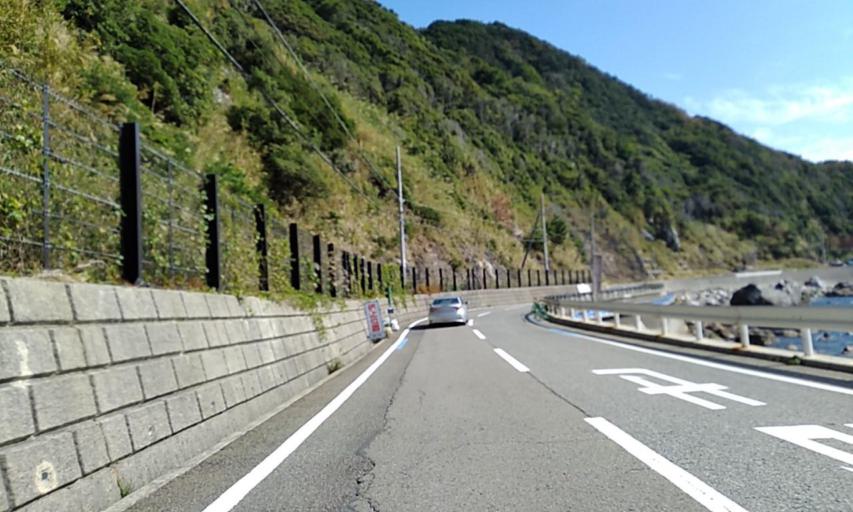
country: JP
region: Wakayama
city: Gobo
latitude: 33.9739
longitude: 135.0770
